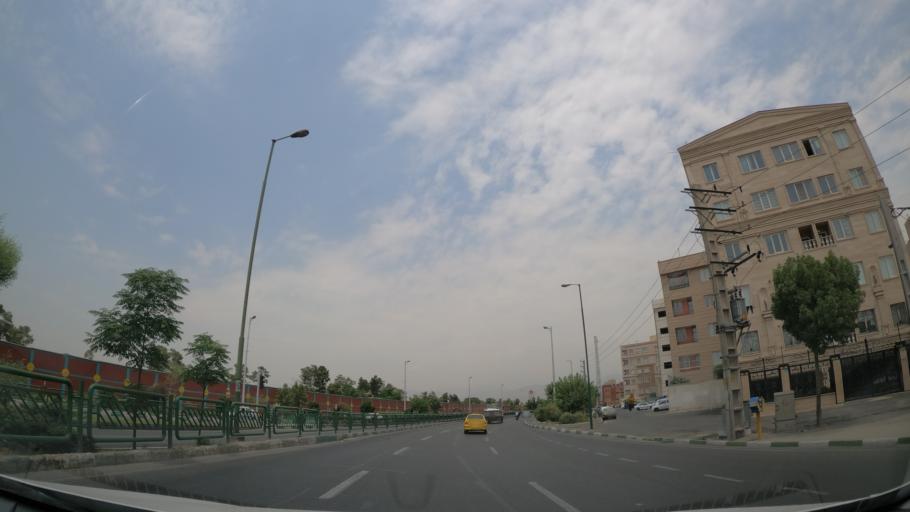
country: IR
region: Tehran
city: Tehran
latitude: 35.6846
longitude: 51.3423
